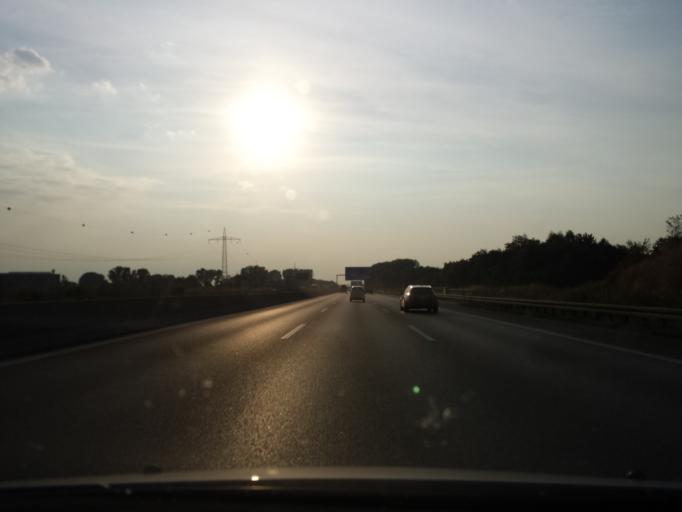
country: DE
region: Bavaria
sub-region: Swabia
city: Augsburg
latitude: 48.4067
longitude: 10.9395
